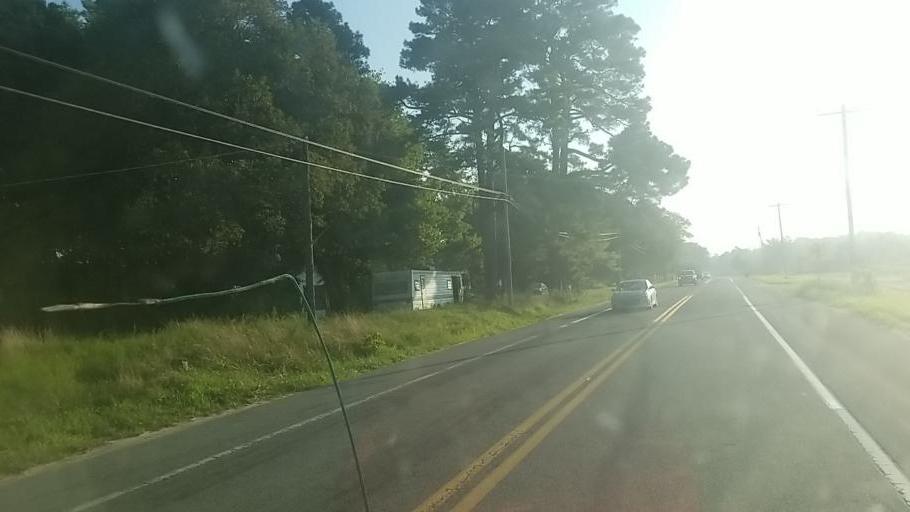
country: US
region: Maryland
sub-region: Worcester County
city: Ocean Pines
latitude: 38.4635
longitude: -75.1270
